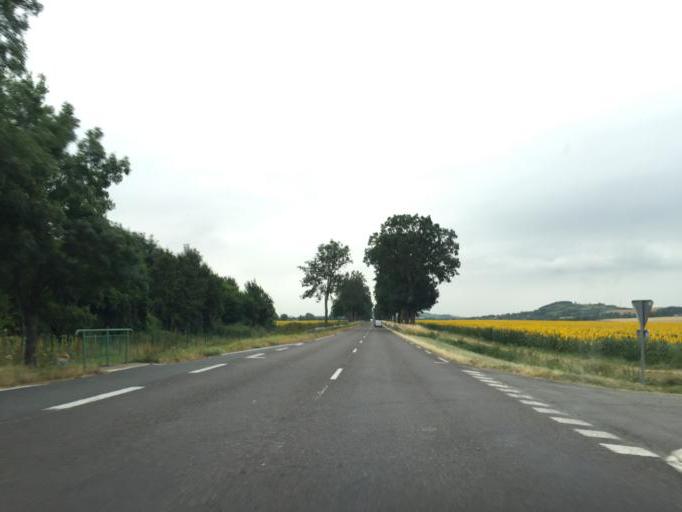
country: FR
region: Auvergne
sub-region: Departement de l'Allier
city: Gannat
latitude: 46.1298
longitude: 3.2085
